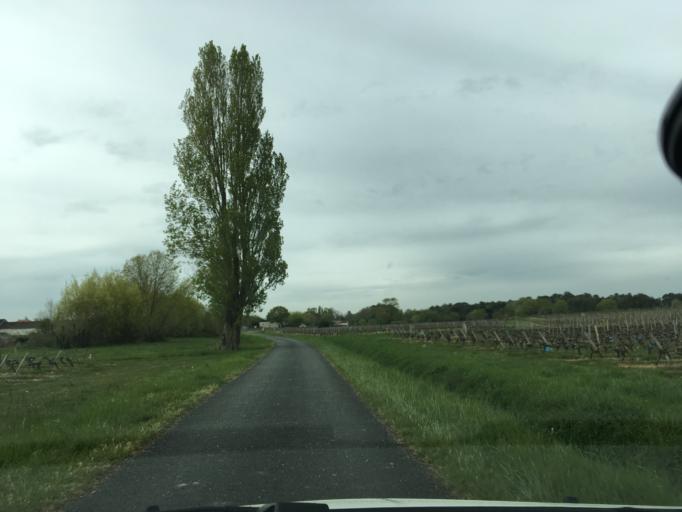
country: FR
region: Aquitaine
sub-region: Departement de la Gironde
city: Lesparre-Medoc
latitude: 45.3172
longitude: -0.8951
